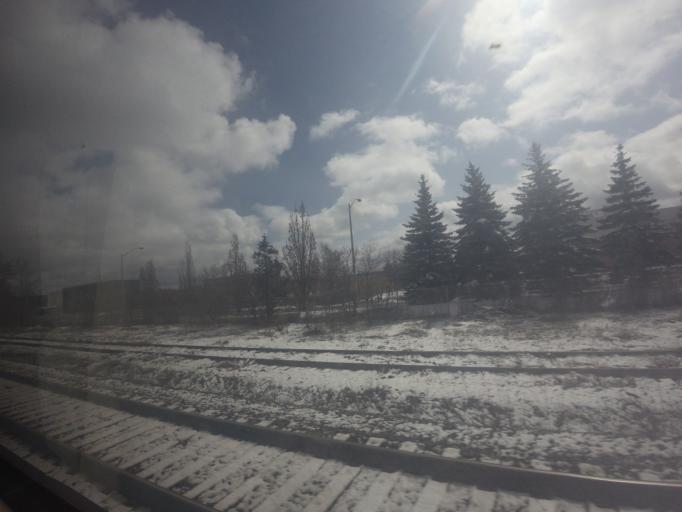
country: CA
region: Ontario
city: Ajax
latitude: 43.8495
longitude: -79.0347
